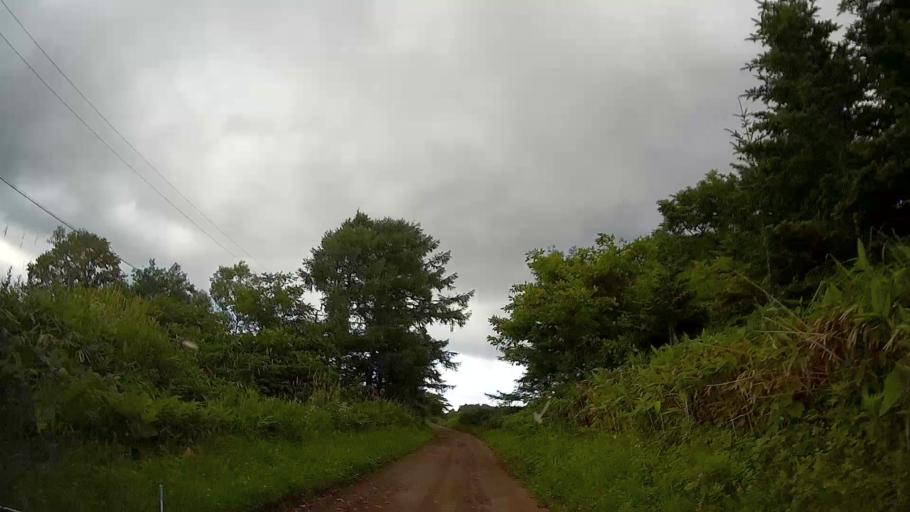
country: JP
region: Hokkaido
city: Nanae
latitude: 42.1234
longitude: 140.4079
